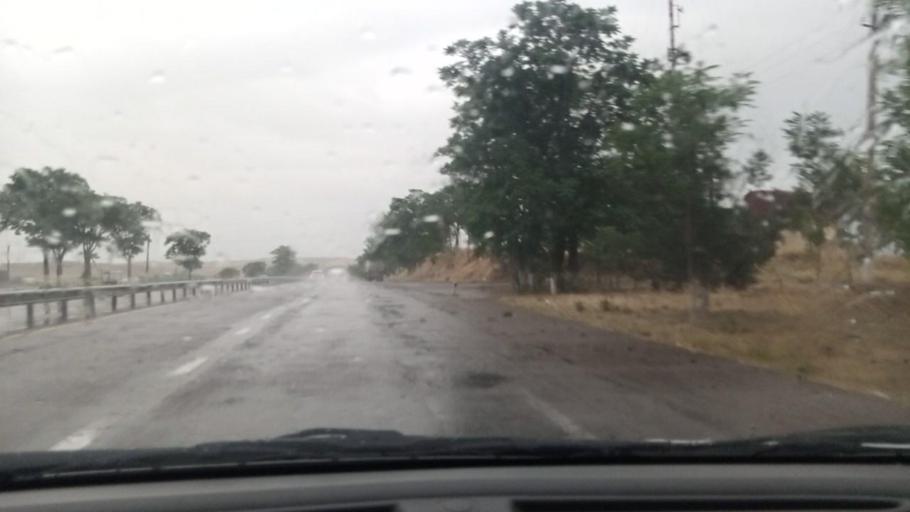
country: UZ
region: Toshkent
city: Ohangaron
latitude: 40.9824
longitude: 69.5391
